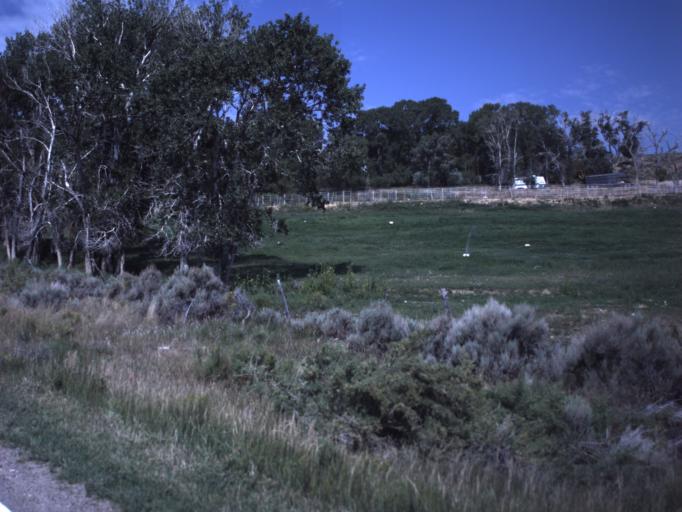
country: US
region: Utah
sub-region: Daggett County
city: Manila
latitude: 40.9787
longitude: -109.7894
